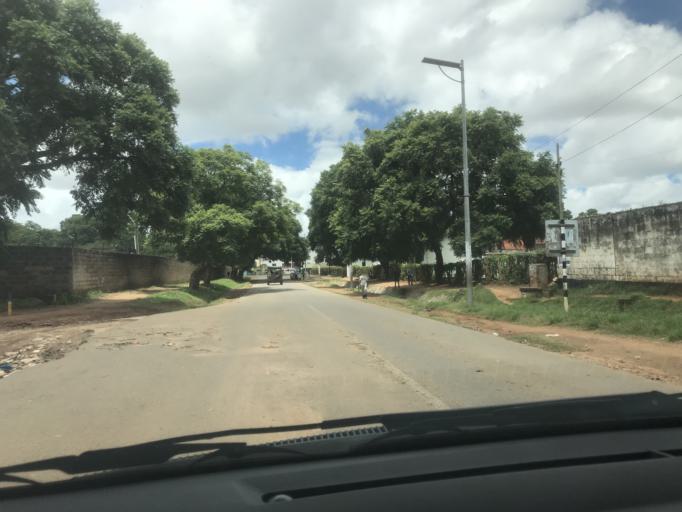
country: ZM
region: Lusaka
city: Lusaka
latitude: -15.4303
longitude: 28.3056
